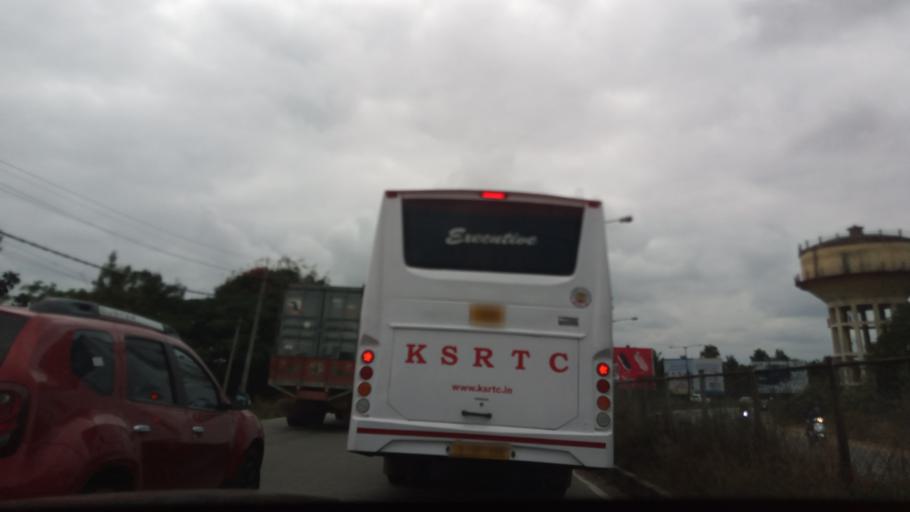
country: IN
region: Karnataka
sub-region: Mandya
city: Shrirangapattana
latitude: 12.4172
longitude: 76.6906
